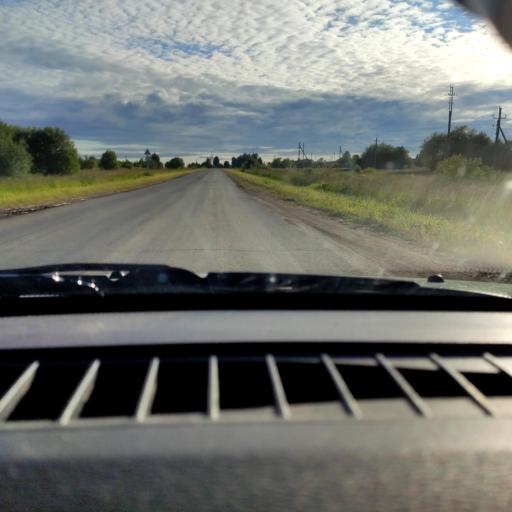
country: RU
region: Perm
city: Uinskoye
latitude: 57.0956
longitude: 56.6418
